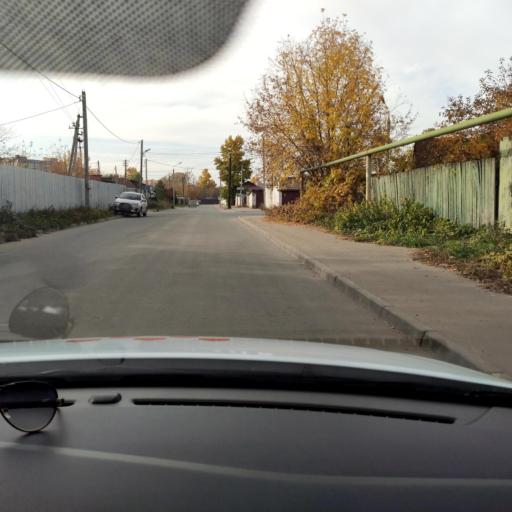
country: RU
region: Tatarstan
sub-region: Gorod Kazan'
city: Kazan
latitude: 55.8065
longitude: 49.0624
